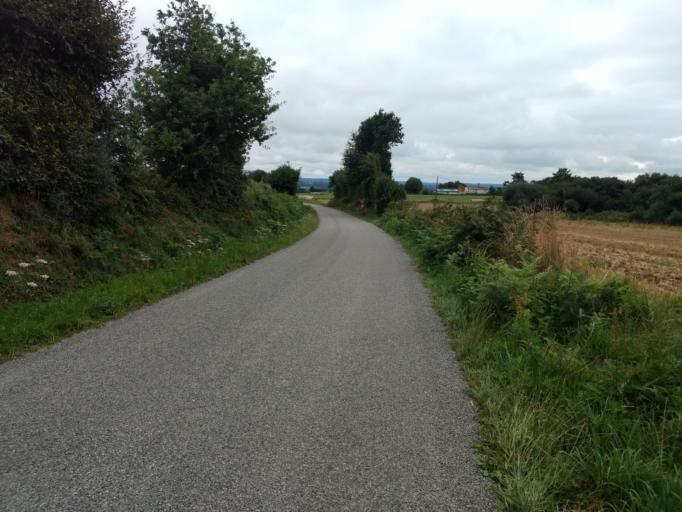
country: FR
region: Brittany
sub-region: Departement du Finistere
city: Loperhet
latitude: 48.3661
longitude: -4.2898
